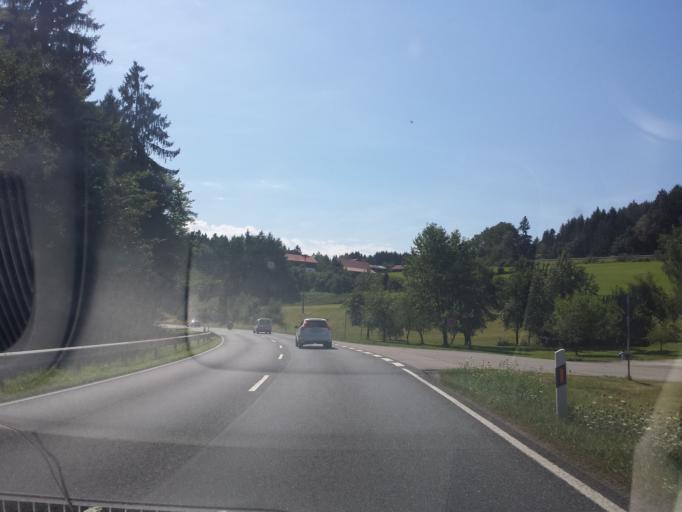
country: DE
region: Bavaria
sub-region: Lower Bavaria
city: Loitzendorf
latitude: 49.1122
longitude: 12.6485
